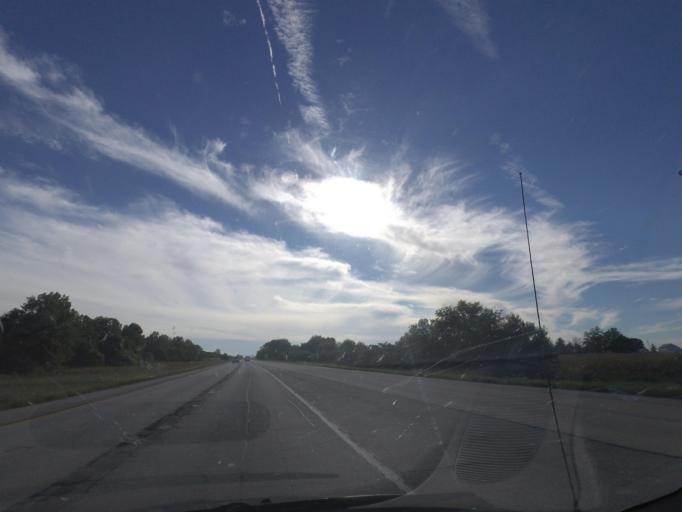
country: US
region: Illinois
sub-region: Macon County
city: Forsyth
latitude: 39.9048
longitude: -88.9939
